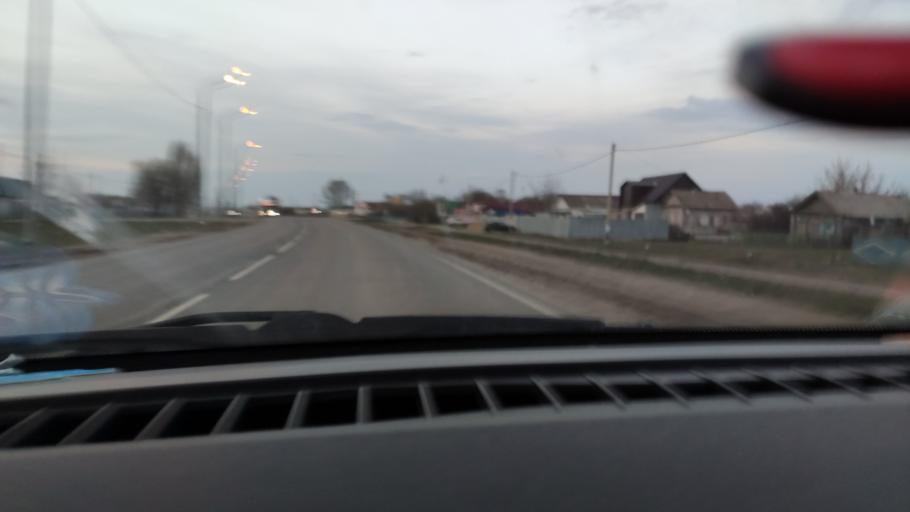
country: RU
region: Saratov
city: Sinodskoye
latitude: 51.9861
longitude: 46.6638
